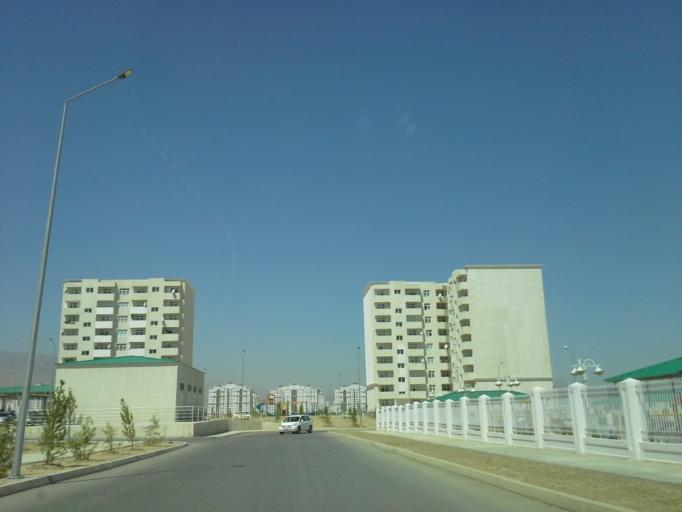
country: TM
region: Ahal
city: Ashgabat
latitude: 37.8869
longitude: 58.4082
